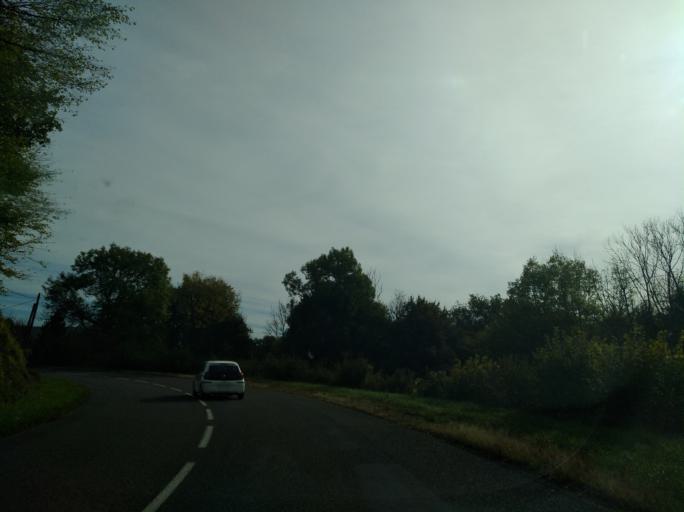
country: FR
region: Bourgogne
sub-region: Departement de Saone-et-Loire
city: Cuiseaux
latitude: 46.4502
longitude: 5.4179
